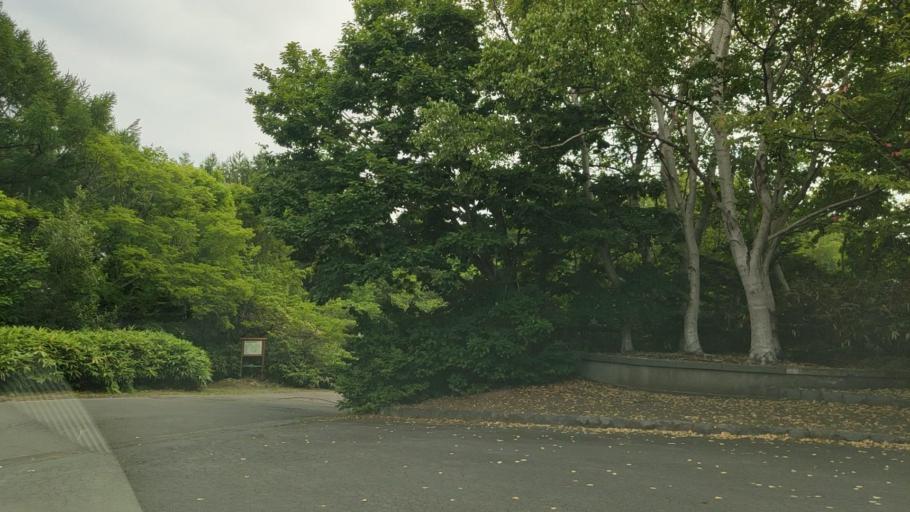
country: JP
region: Hokkaido
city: Otaru
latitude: 43.1968
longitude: 140.9826
